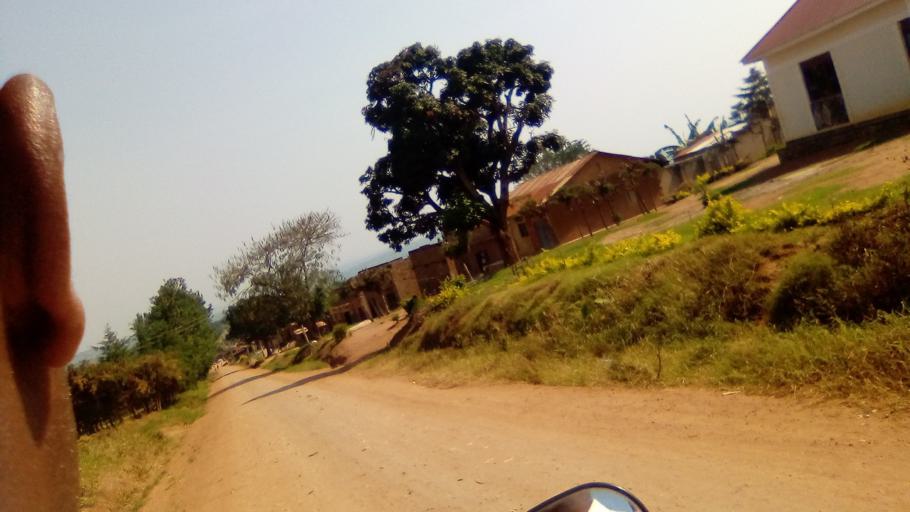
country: UG
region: Central Region
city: Masaka
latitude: -0.2712
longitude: 31.6455
